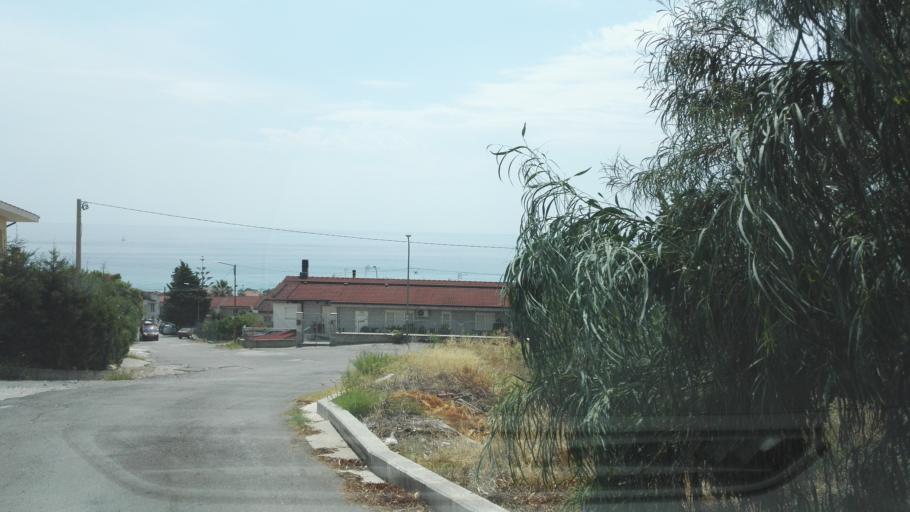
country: IT
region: Calabria
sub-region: Provincia di Reggio Calabria
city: Riace Marina
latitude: 38.3921
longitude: 16.5248
